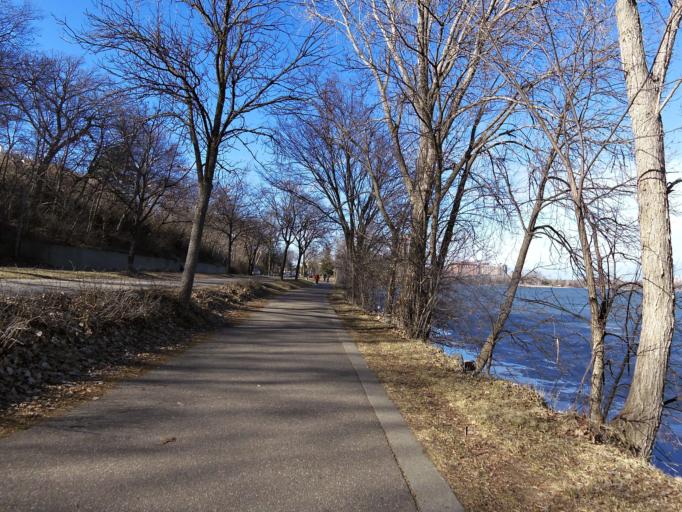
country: US
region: Minnesota
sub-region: Hennepin County
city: Saint Louis Park
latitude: 44.9422
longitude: -93.3201
